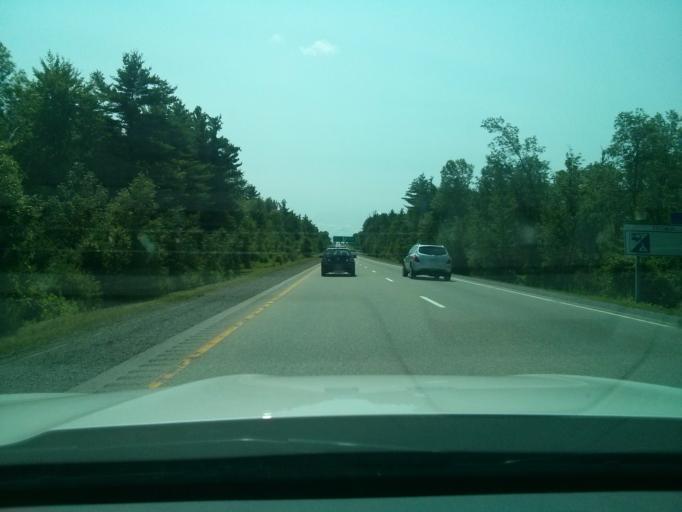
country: CA
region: Ontario
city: Prescott
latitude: 44.7795
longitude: -75.5067
